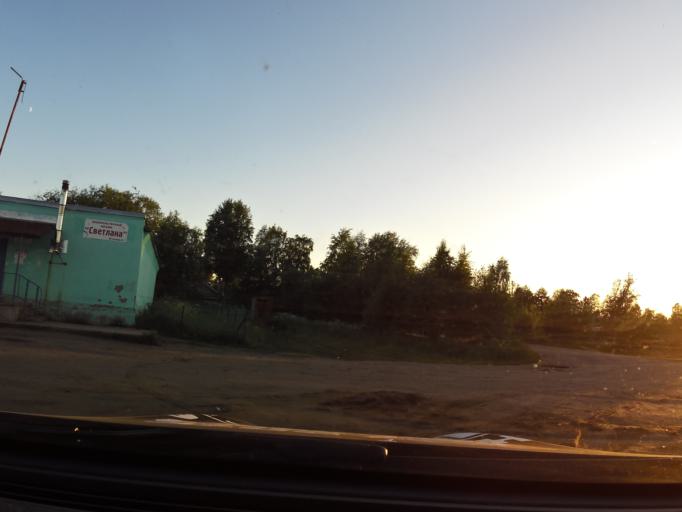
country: RU
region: Leningrad
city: Voznesen'ye
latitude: 61.0138
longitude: 35.4852
